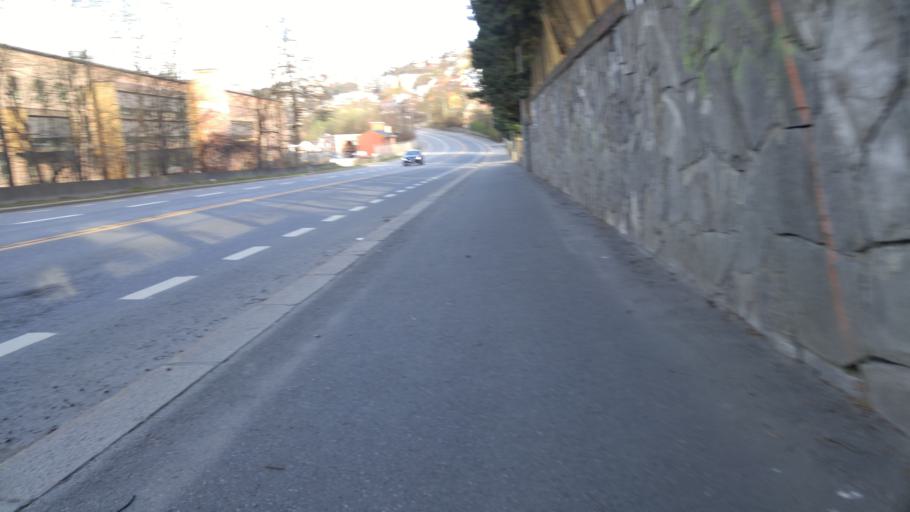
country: NO
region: Oslo
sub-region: Oslo
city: Oslo
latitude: 59.9042
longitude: 10.7733
